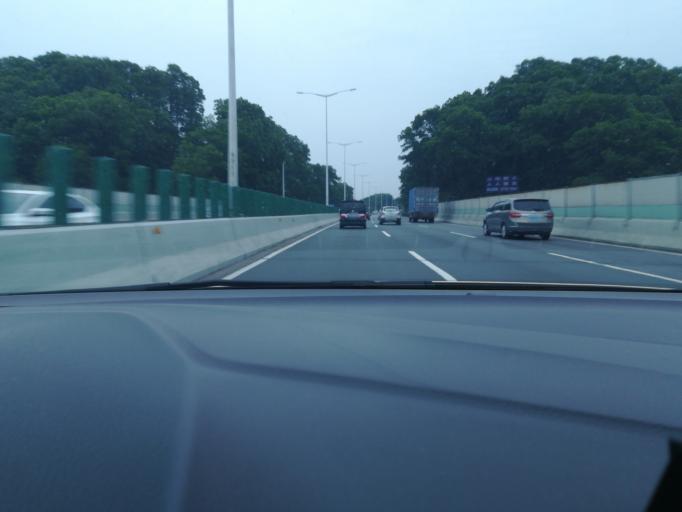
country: CN
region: Guangdong
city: Taihe
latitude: 23.2617
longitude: 113.3581
